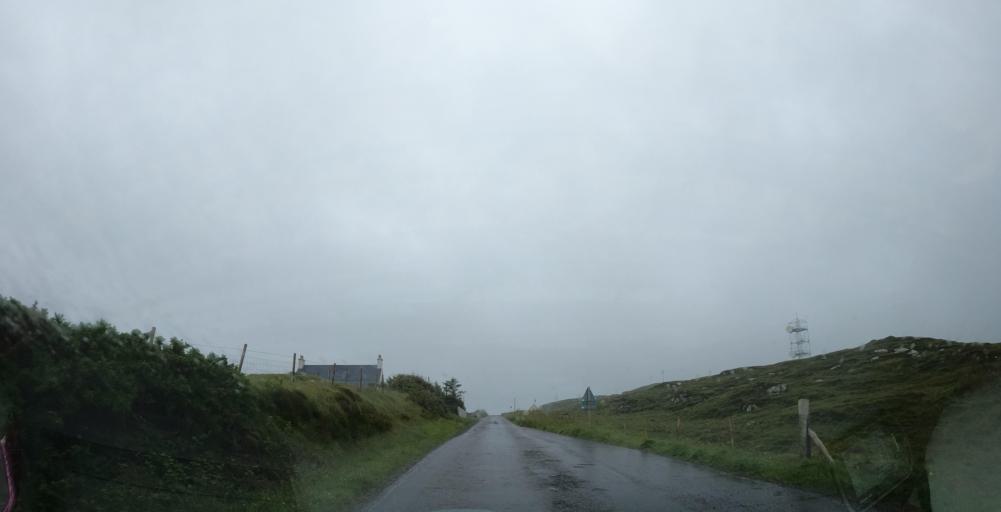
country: GB
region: Scotland
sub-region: Eilean Siar
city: Barra
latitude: 56.9897
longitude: -7.4179
